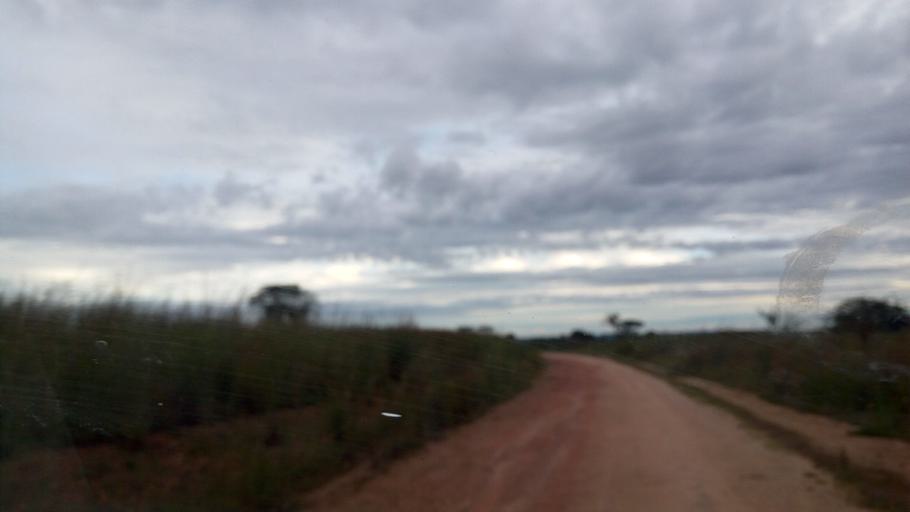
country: CD
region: Katanga
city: Kalemie
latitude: -6.8380
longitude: 29.1555
